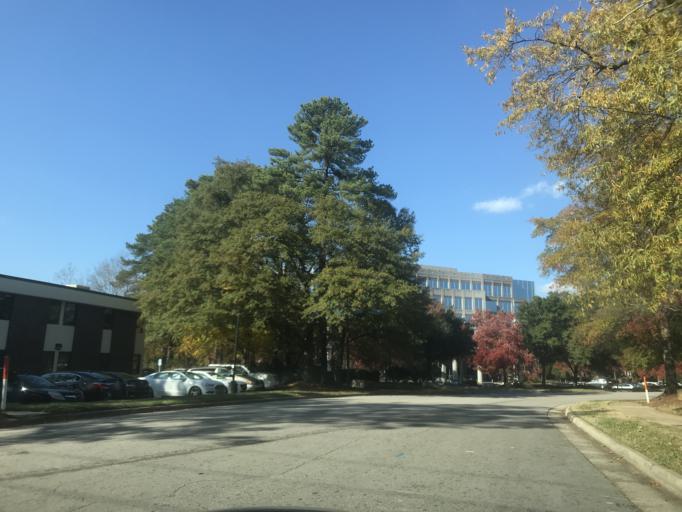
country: US
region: North Carolina
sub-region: Wake County
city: Raleigh
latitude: 35.8282
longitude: -78.6221
